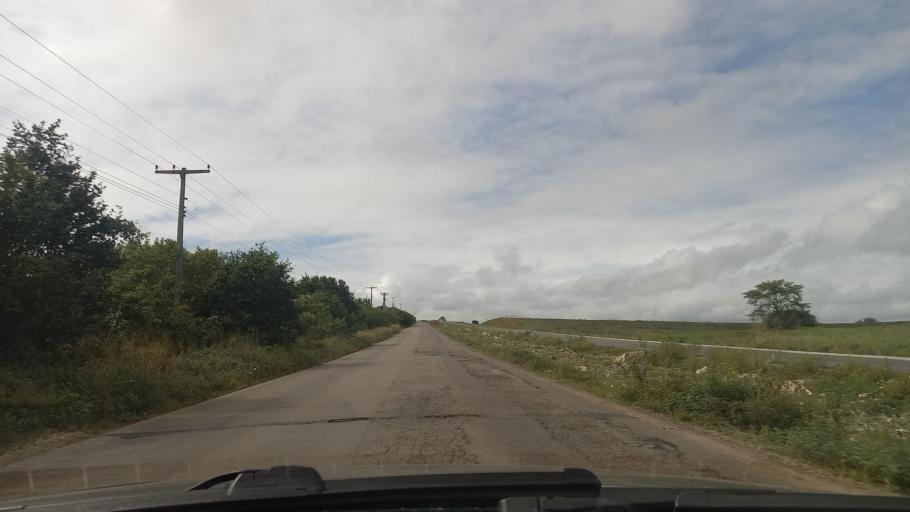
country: BR
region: Alagoas
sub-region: Batalha
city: Batalha
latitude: -9.6602
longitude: -37.1726
